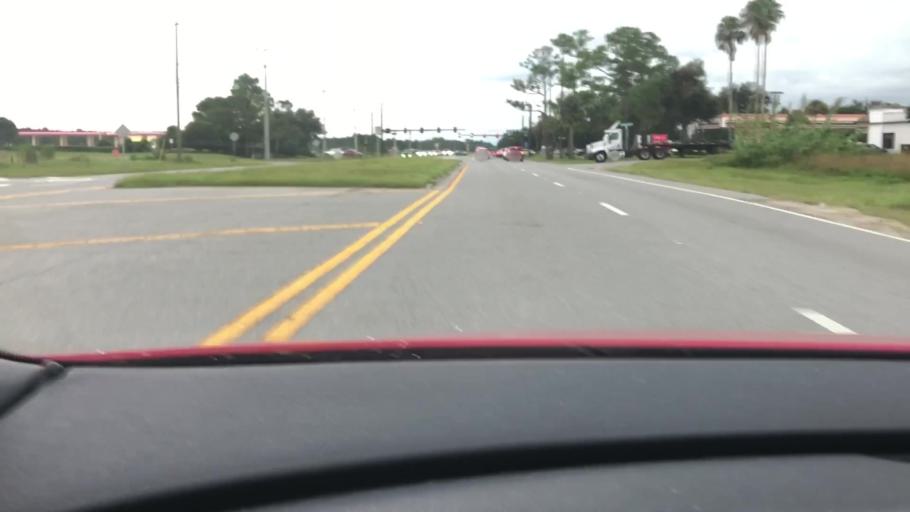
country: US
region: Florida
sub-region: Volusia County
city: Holly Hill
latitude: 29.2236
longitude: -81.0964
